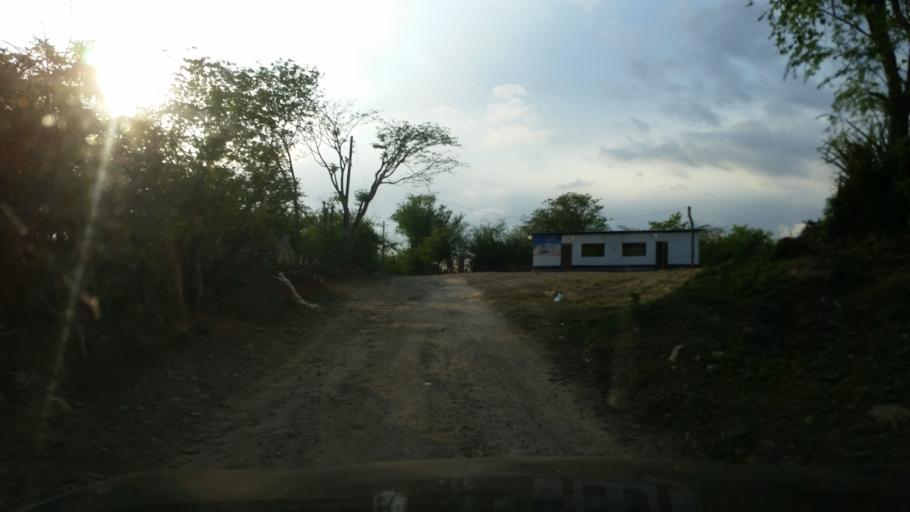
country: NI
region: Managua
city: Masachapa
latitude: 11.7987
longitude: -86.4724
